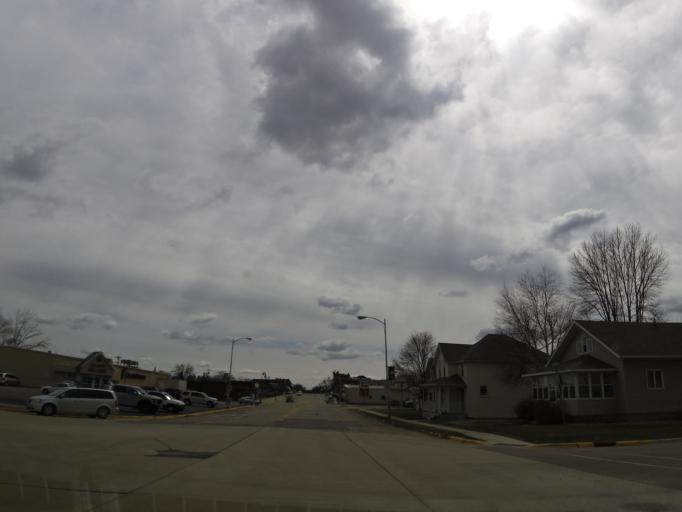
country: US
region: Minnesota
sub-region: Goodhue County
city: Pine Island
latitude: 44.2045
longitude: -92.6463
